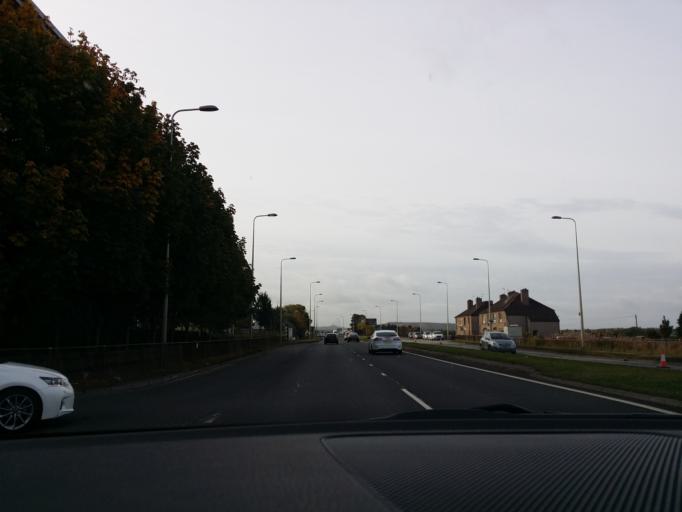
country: GB
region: Scotland
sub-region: Edinburgh
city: Newbridge
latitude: 55.9388
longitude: -3.3918
